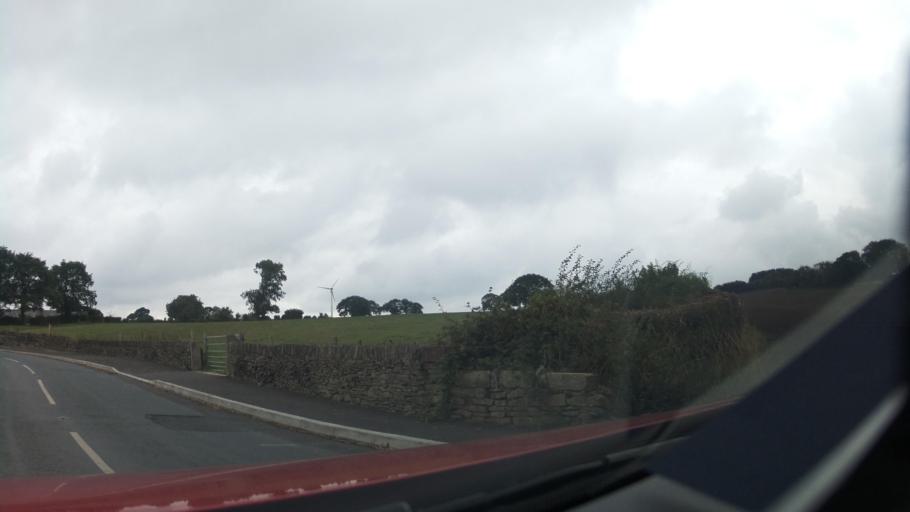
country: GB
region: England
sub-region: Kirklees
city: Shelley
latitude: 53.5995
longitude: -1.6807
